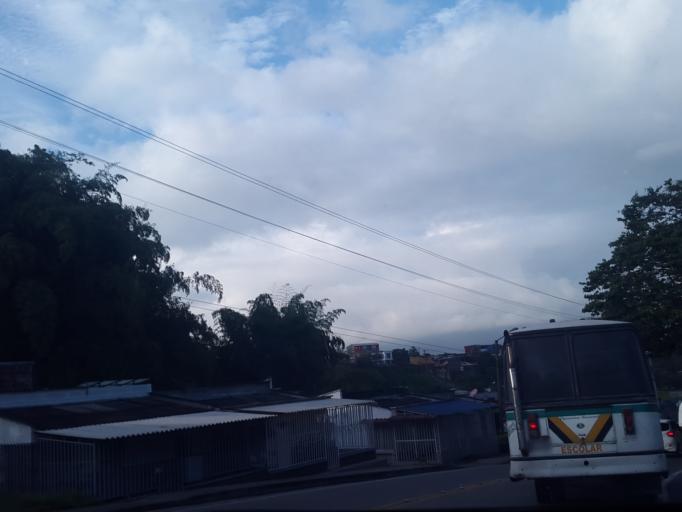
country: CO
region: Quindio
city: Calarca
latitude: 4.5347
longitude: -75.6409
